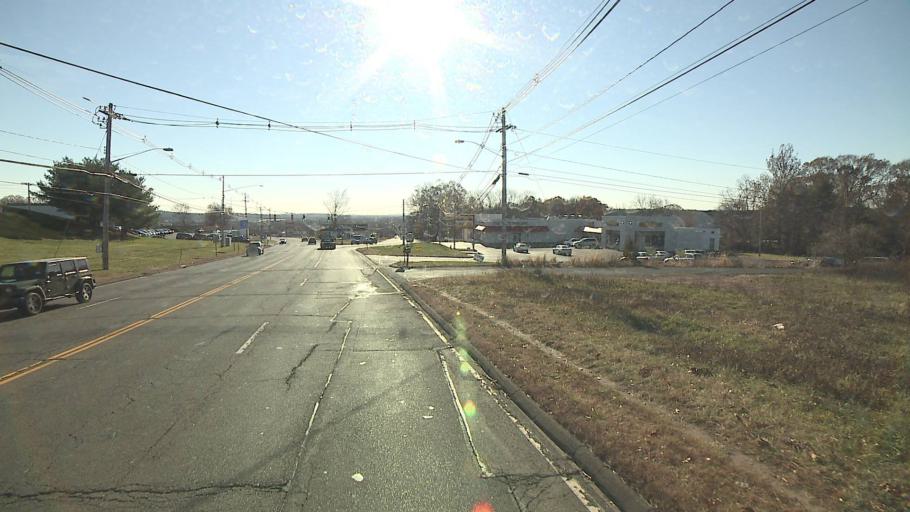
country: US
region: Connecticut
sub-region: New Haven County
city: Meriden
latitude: 41.5053
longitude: -72.8104
